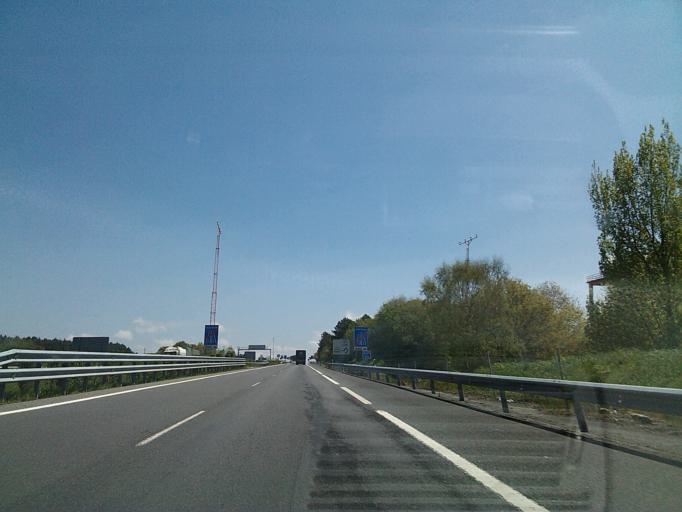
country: ES
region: Galicia
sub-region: Provincia da Coruna
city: Oroso
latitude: 42.9138
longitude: -8.4212
